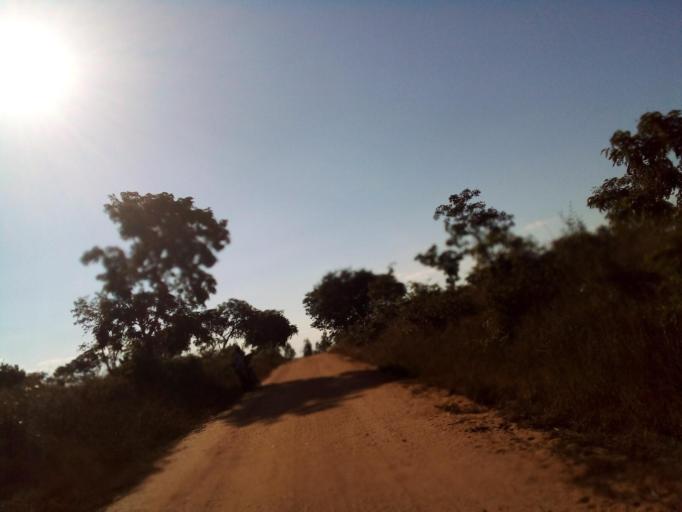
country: MZ
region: Zambezia
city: Quelimane
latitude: -17.5012
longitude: 36.5801
